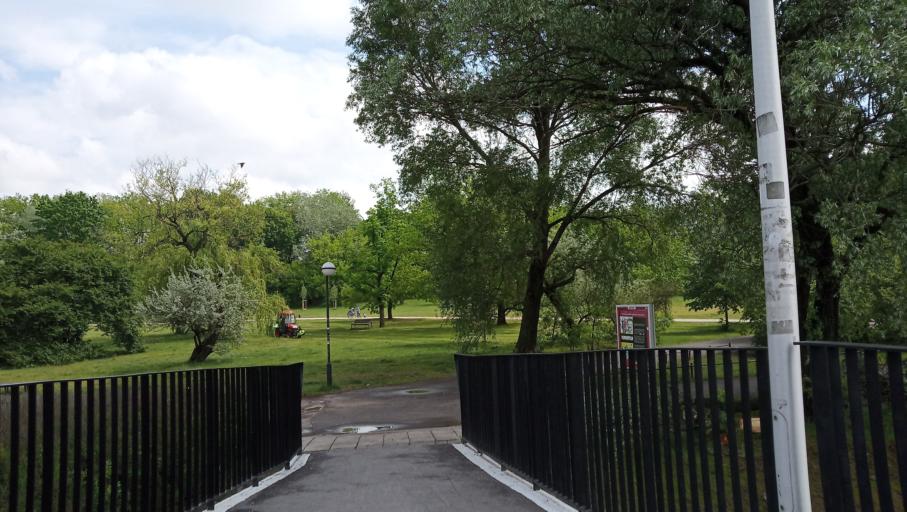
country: PL
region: Masovian Voivodeship
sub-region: Warszawa
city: Zoliborz
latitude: 52.2763
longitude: 20.9913
